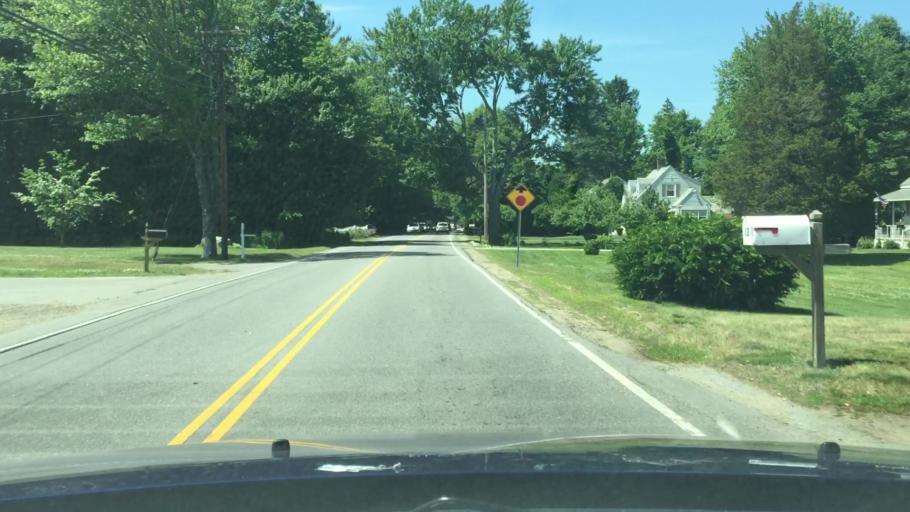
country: US
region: New Hampshire
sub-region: Rockingham County
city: Plaistow
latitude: 42.8161
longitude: -71.0950
